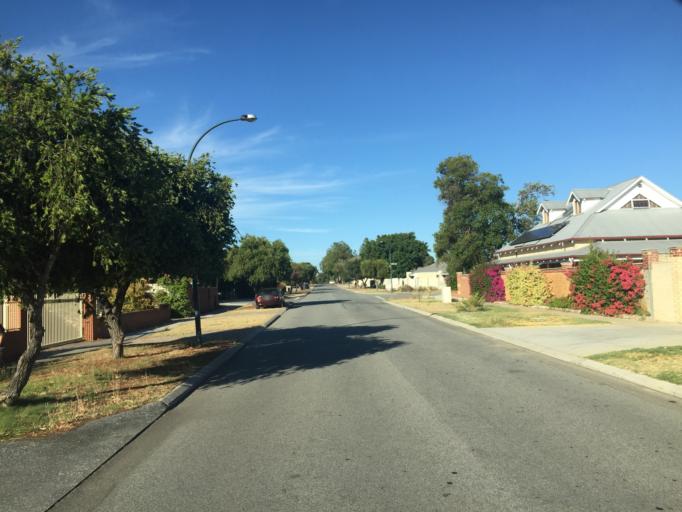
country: AU
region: Western Australia
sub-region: Belmont
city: Rivervale
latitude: -31.9634
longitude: 115.9164
